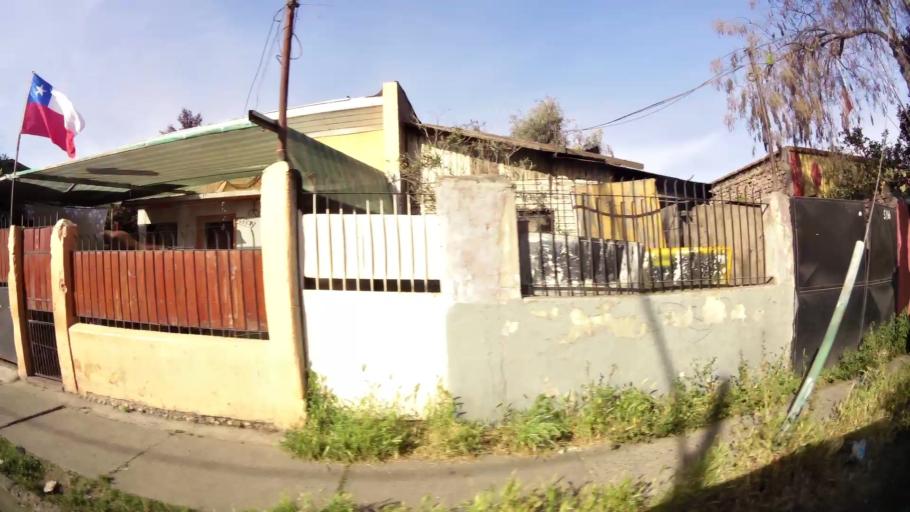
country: CL
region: Santiago Metropolitan
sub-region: Provincia de Santiago
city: Santiago
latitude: -33.5122
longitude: -70.6343
